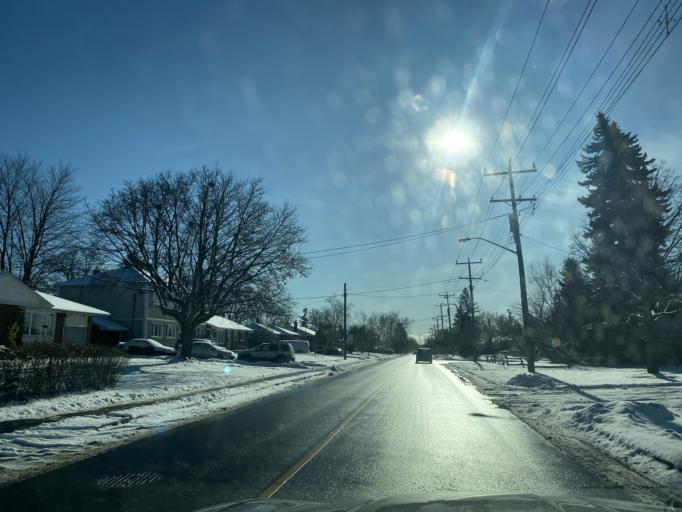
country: CA
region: Ontario
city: Scarborough
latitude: 43.7742
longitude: -79.3166
